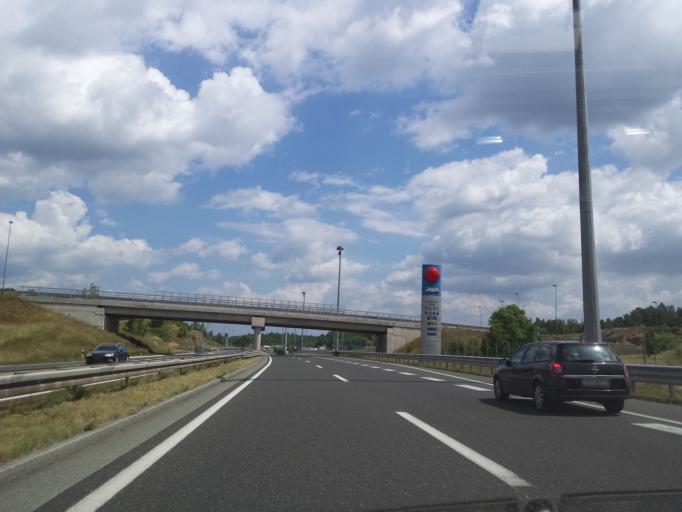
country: HR
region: Karlovacka
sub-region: Grad Karlovac
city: Karlovac
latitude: 45.4525
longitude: 15.3742
